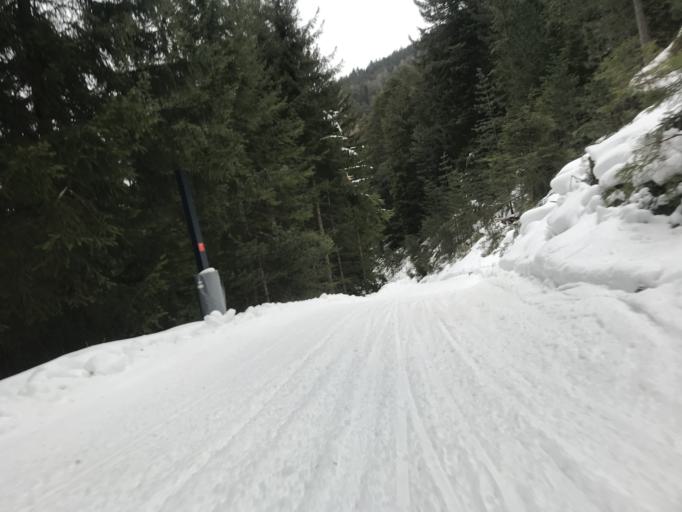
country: IT
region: Trentino-Alto Adige
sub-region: Bolzano
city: Funes - Villnoess
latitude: 46.6821
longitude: 11.6843
